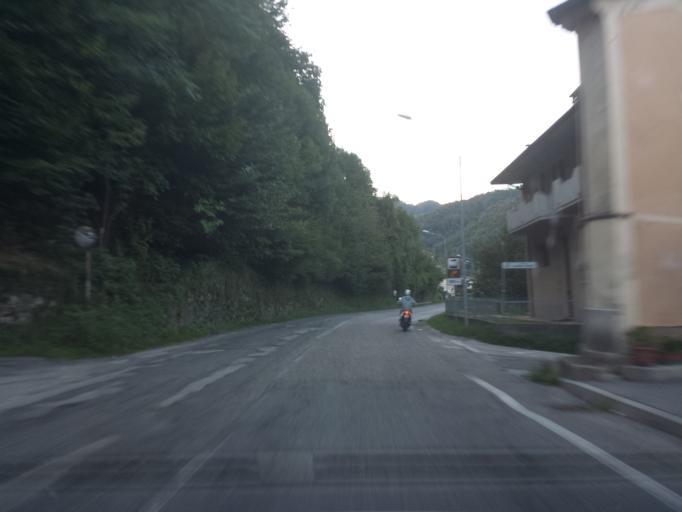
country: IT
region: Veneto
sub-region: Provincia di Vicenza
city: Recoaro Terme
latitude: 45.6977
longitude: 11.2511
